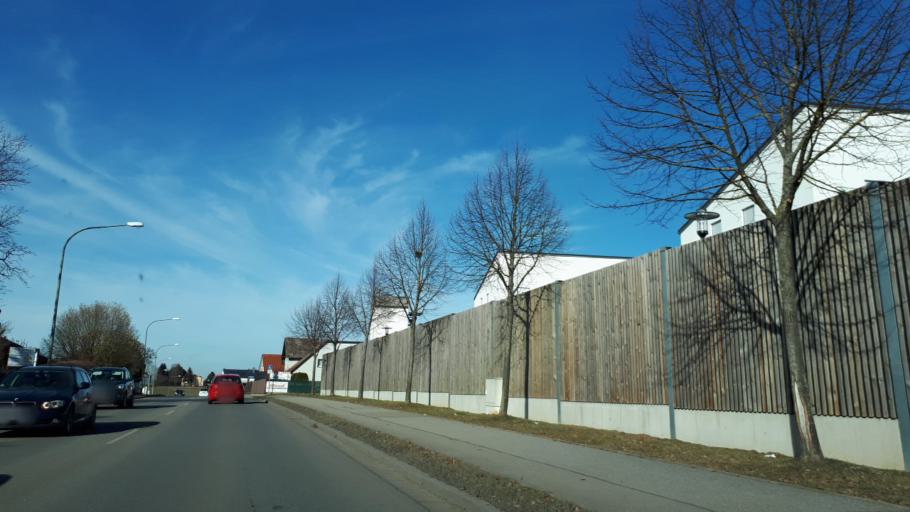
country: DE
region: Bavaria
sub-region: Upper Palatinate
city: Pentling
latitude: 48.9820
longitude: 12.0661
